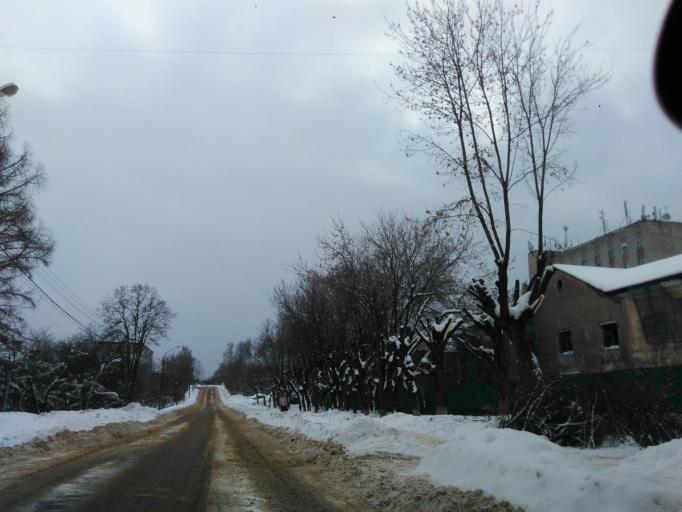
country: RU
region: Moskovskaya
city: Yakhroma
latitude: 56.2783
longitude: 37.4835
